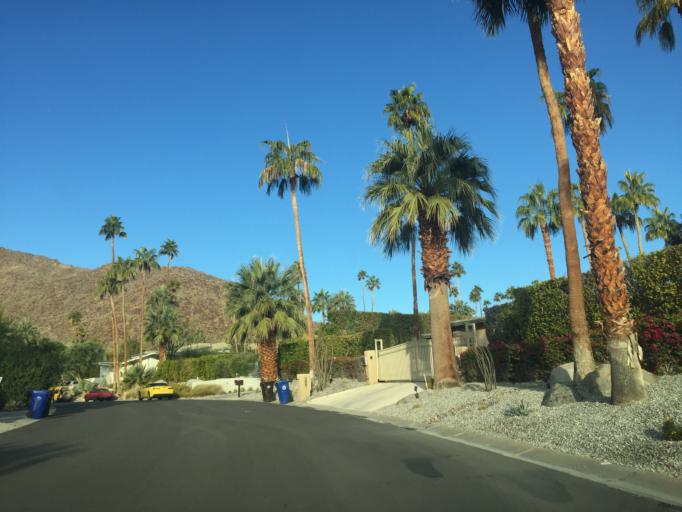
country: US
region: California
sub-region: Riverside County
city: Palm Springs
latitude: 33.8406
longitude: -116.5556
